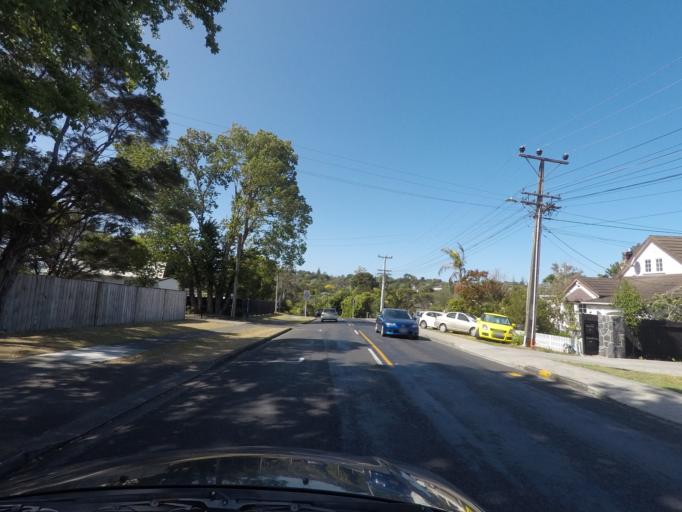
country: NZ
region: Auckland
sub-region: Auckland
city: Waitakere
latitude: -36.9263
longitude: 174.6548
